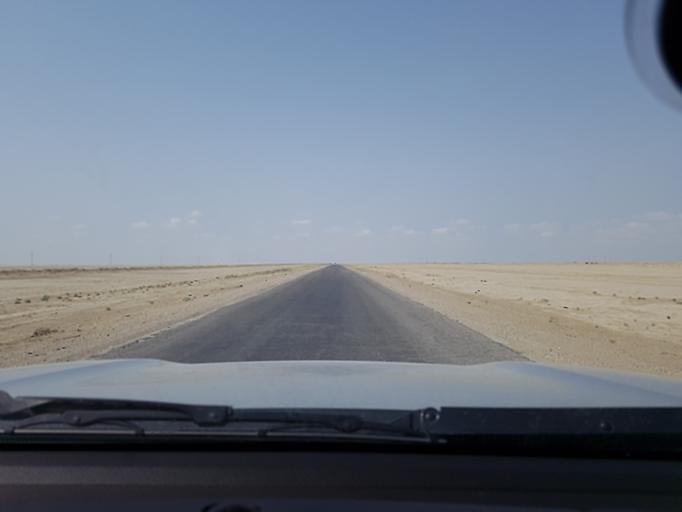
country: TM
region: Balkan
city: Gumdag
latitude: 38.6754
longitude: 54.4103
